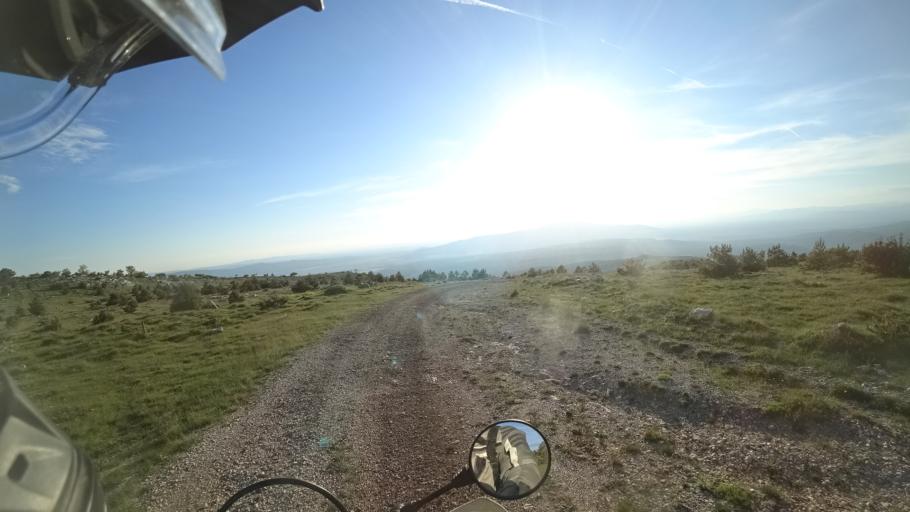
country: HR
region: Sibensko-Kniniska
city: Drnis
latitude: 43.8808
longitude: 16.3412
